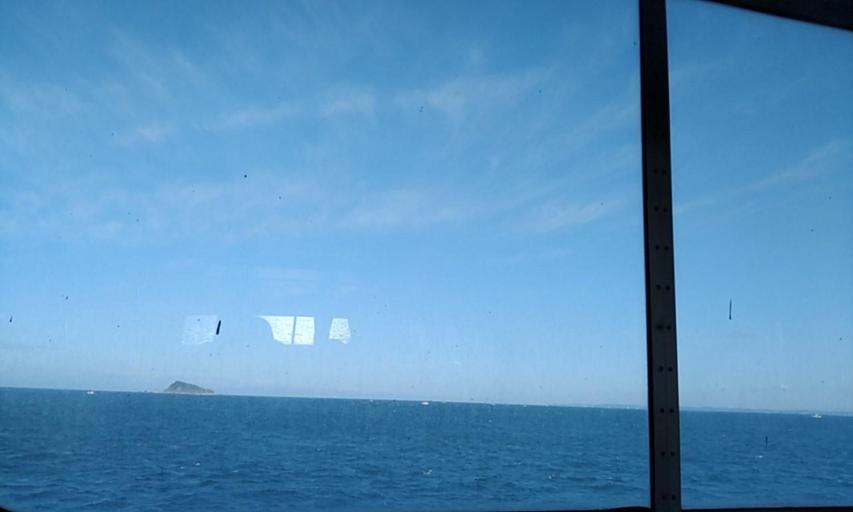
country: JP
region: Mie
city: Toba
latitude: 34.5330
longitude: 136.9485
